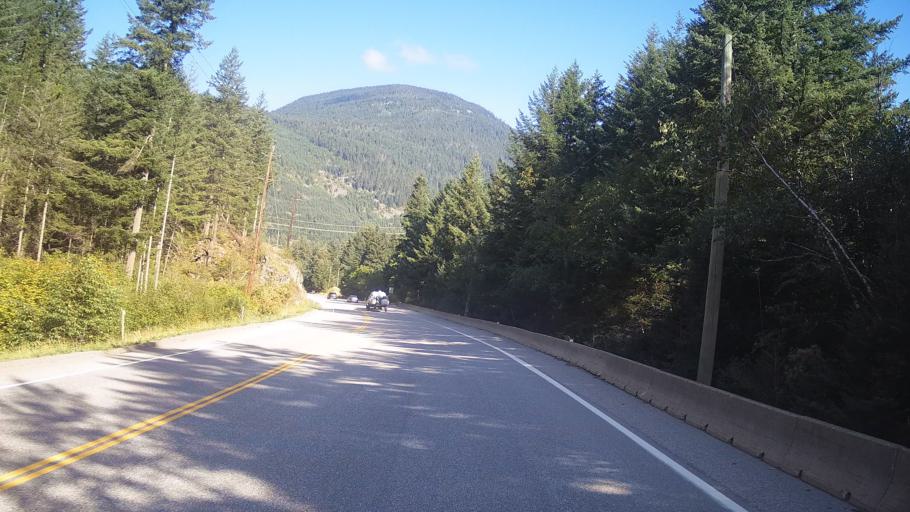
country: CA
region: British Columbia
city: Hope
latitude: 49.6585
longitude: -121.4079
